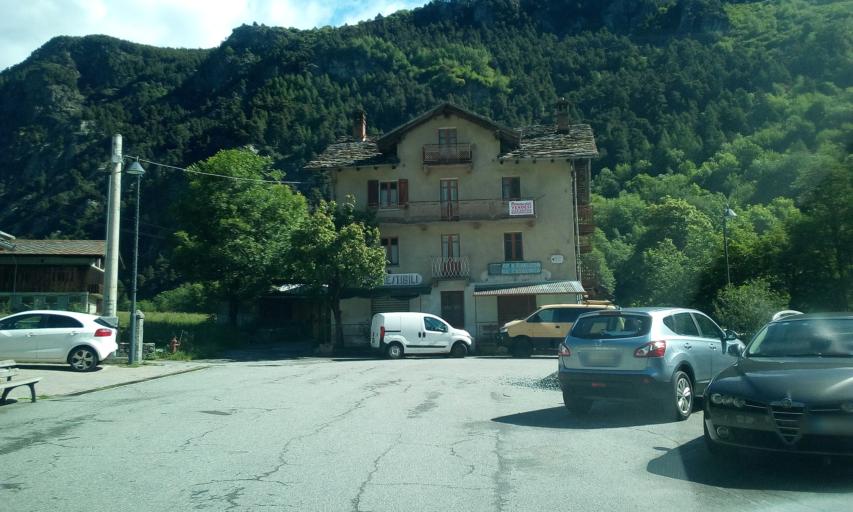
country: IT
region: Aosta Valley
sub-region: Valle d'Aosta
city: Brusson
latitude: 45.7398
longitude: 7.7467
